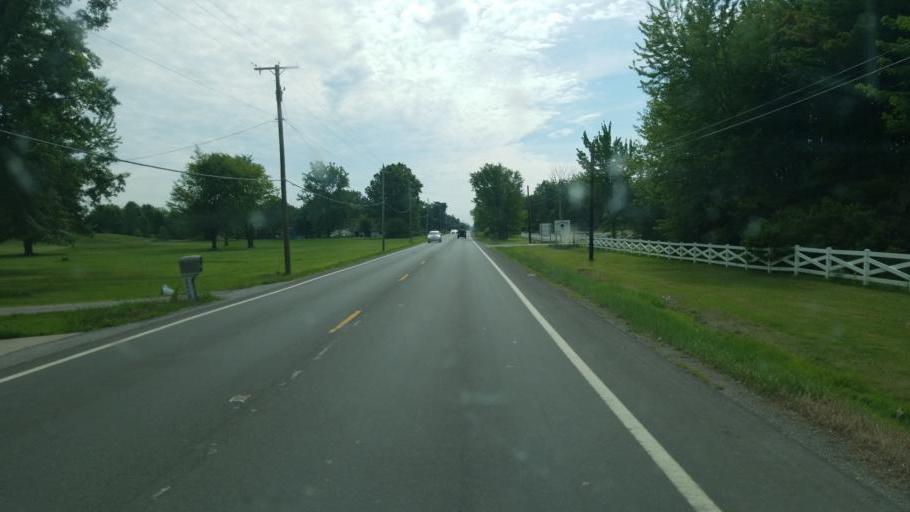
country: US
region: Ohio
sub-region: Cuyahoga County
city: Strongsville
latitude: 41.3125
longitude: -81.8894
